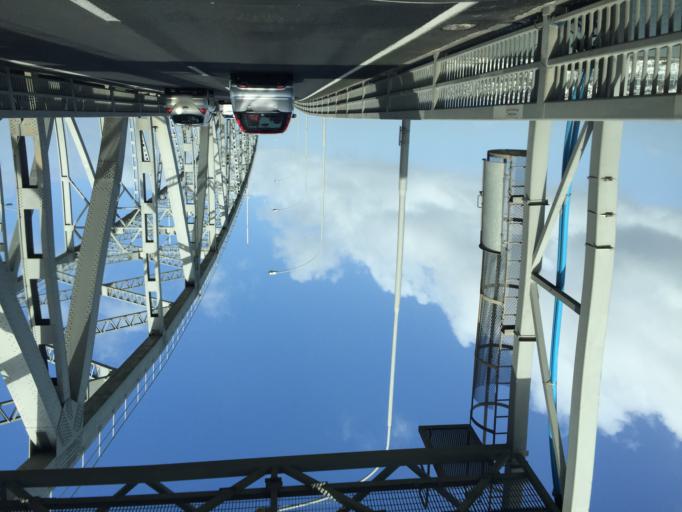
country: NZ
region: Auckland
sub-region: Auckland
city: North Shore
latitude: -36.8283
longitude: 174.7474
